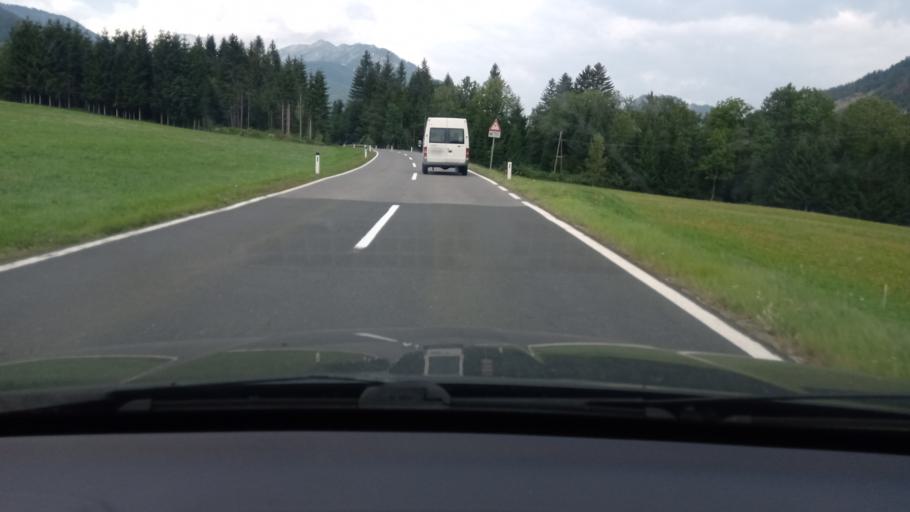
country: AT
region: Carinthia
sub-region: Politischer Bezirk Hermagor
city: Hermagor
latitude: 46.6715
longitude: 13.2851
